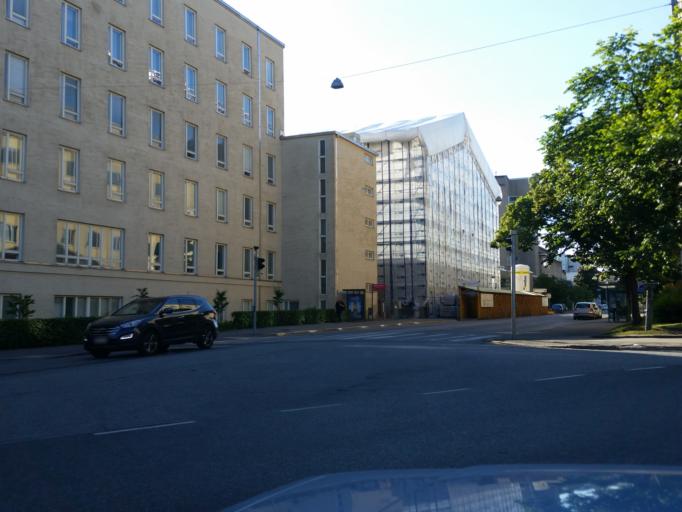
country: FI
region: Uusimaa
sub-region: Helsinki
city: Helsinki
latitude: 60.1890
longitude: 24.9120
